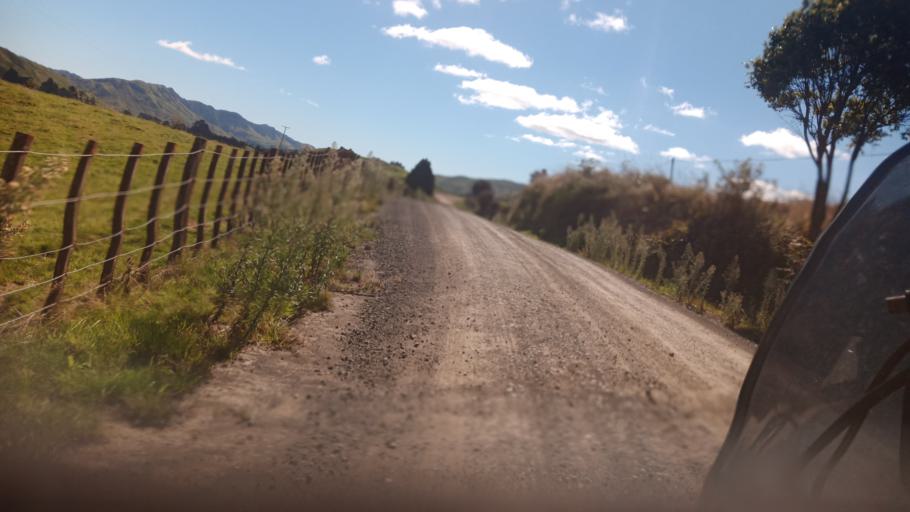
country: NZ
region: Bay of Plenty
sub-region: Opotiki District
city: Opotiki
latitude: -38.3049
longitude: 177.5619
